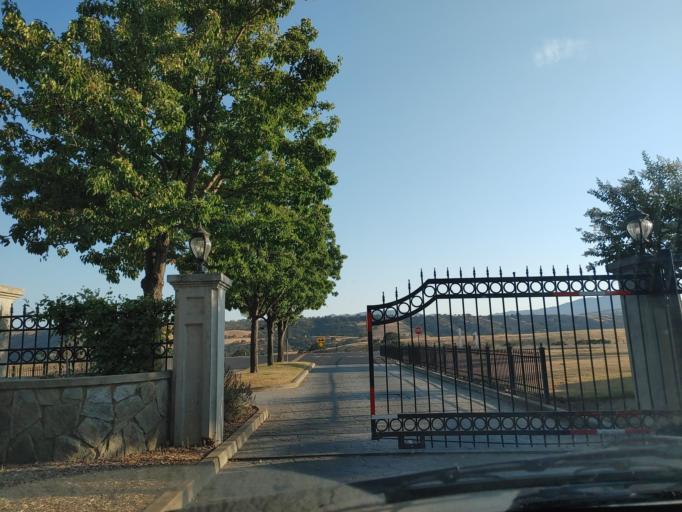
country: US
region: California
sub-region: San Benito County
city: Ridgemark
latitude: 36.7957
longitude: -121.3265
